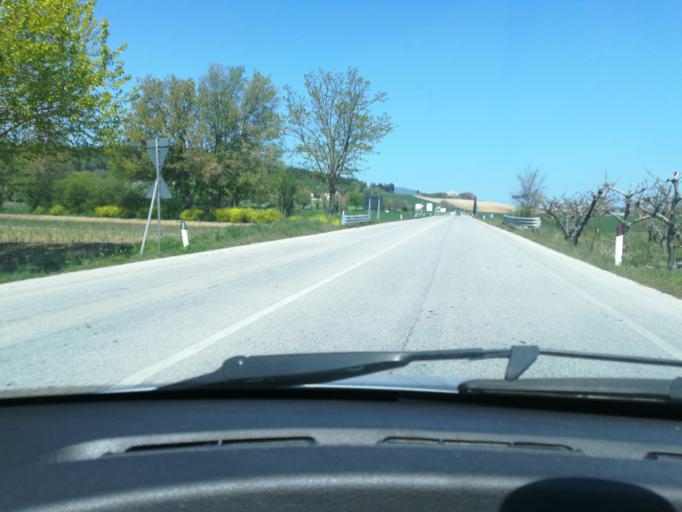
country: IT
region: The Marches
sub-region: Provincia di Ancona
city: Villa Musone
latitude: 43.4569
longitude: 13.5964
